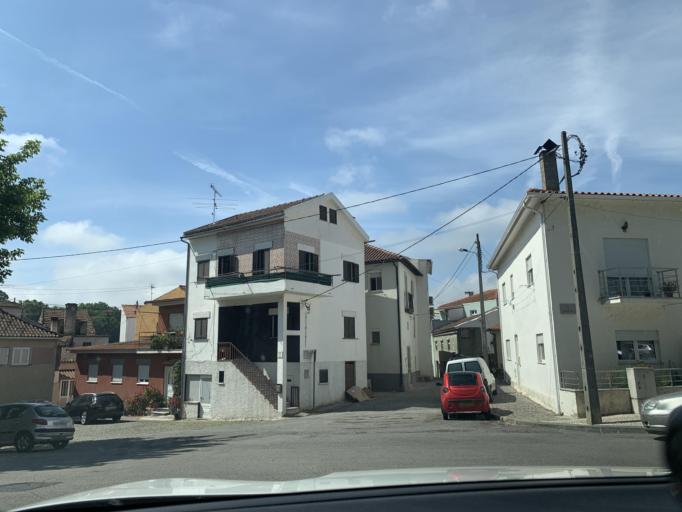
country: PT
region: Viseu
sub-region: Viseu
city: Viseu
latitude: 40.6528
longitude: -7.9255
